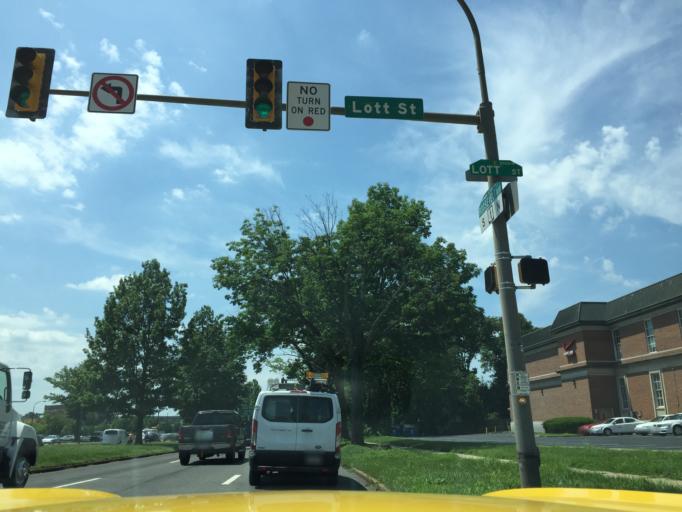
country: US
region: Pennsylvania
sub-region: Bucks County
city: Feasterville
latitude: 40.0849
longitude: -75.0252
